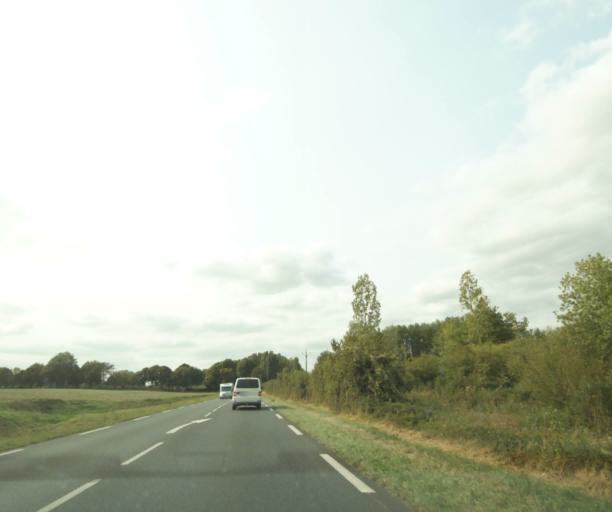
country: FR
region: Centre
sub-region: Departement de l'Indre
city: Chatillon-sur-Indre
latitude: 46.9682
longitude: 1.1992
